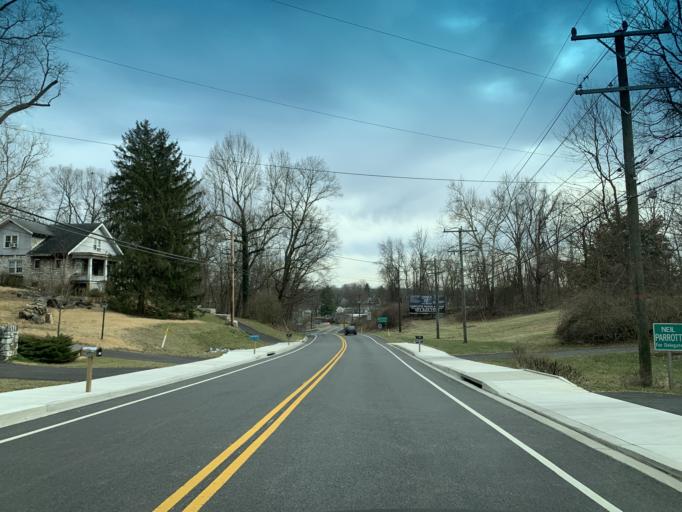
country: US
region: Maryland
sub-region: Washington County
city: Hagerstown
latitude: 39.6142
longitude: -77.7111
